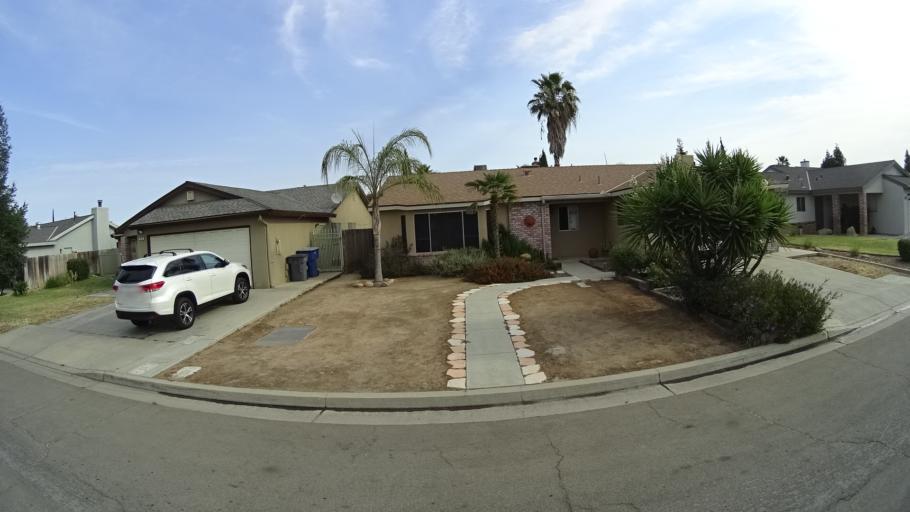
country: US
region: California
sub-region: Fresno County
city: West Park
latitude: 36.7751
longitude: -119.8747
